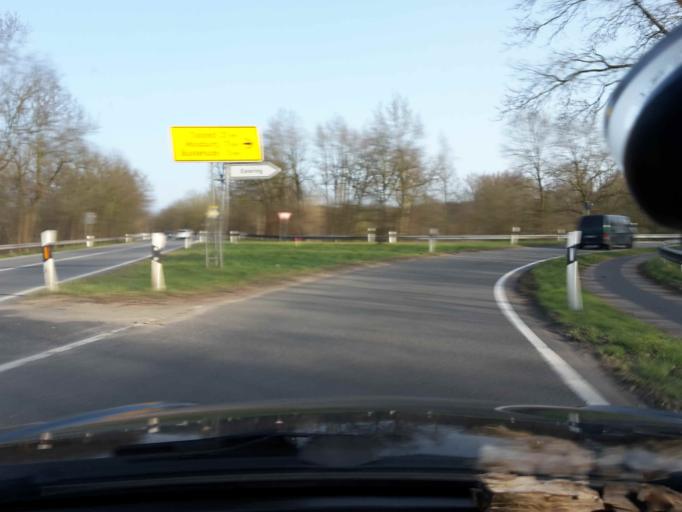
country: DE
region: Lower Saxony
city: Buxtehude
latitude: 53.4614
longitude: 9.6935
